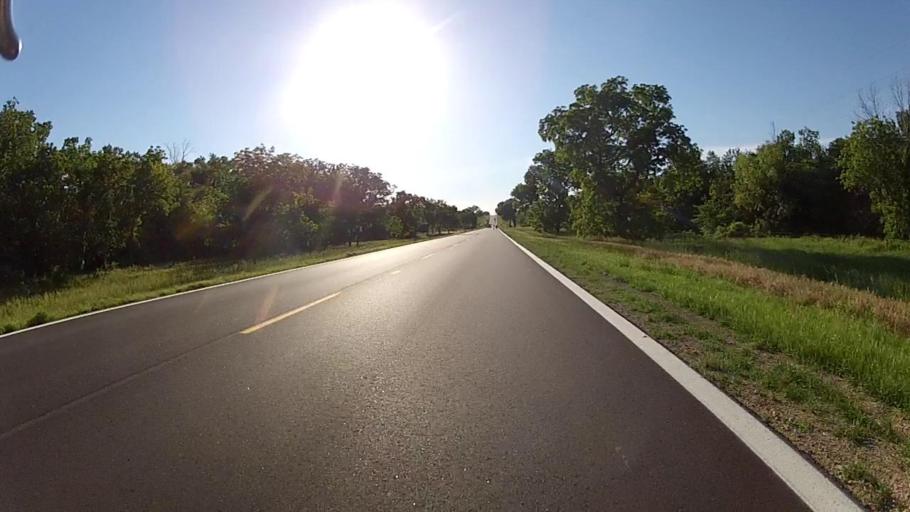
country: US
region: Kansas
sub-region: Comanche County
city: Coldwater
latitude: 37.2819
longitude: -99.0793
